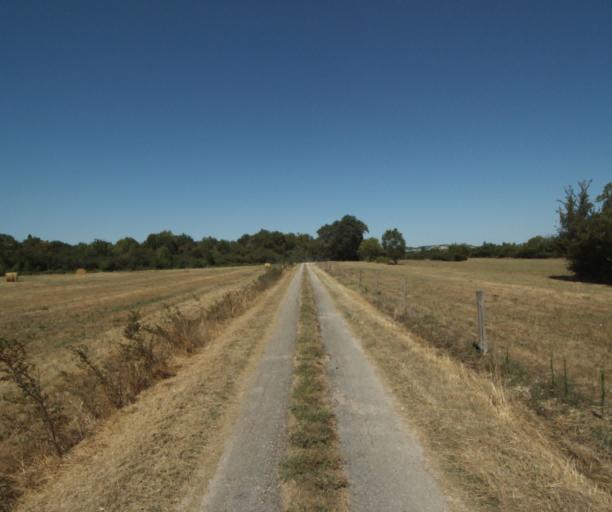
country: FR
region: Midi-Pyrenees
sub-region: Departement de la Haute-Garonne
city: Revel
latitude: 43.4697
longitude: 1.9851
